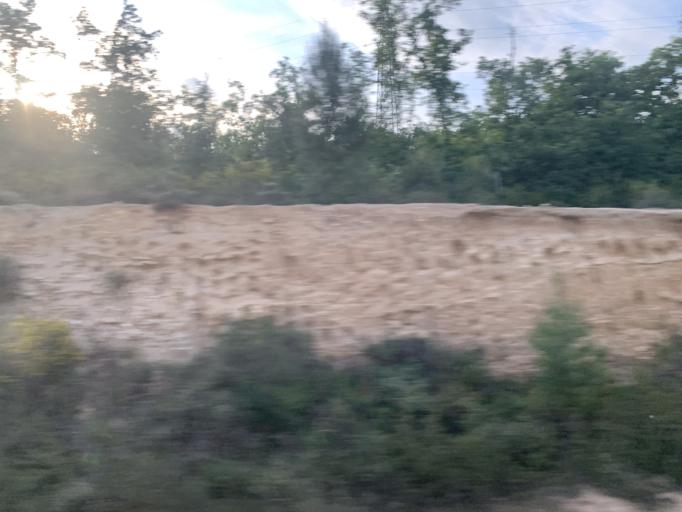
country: ES
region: Catalonia
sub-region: Provincia de Girona
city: Massanes
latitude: 41.7589
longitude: 2.6609
